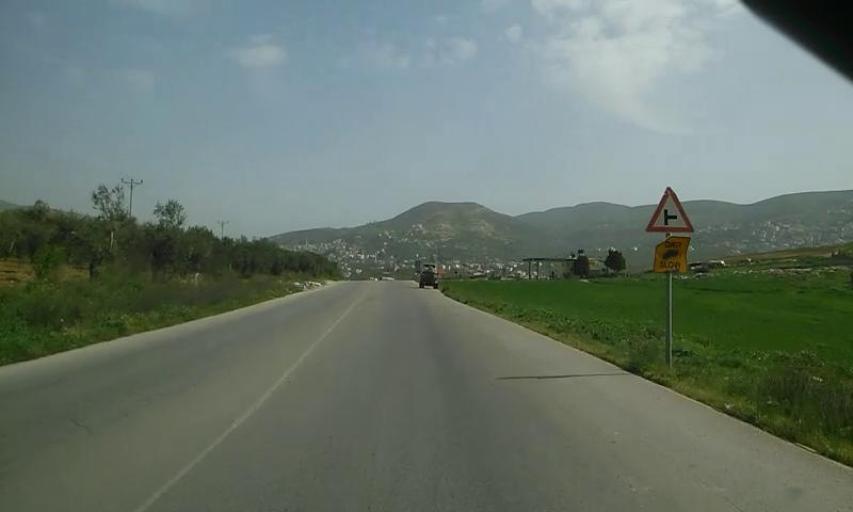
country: PS
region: West Bank
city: Al Fandaqumiyah
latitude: 32.3396
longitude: 35.2037
